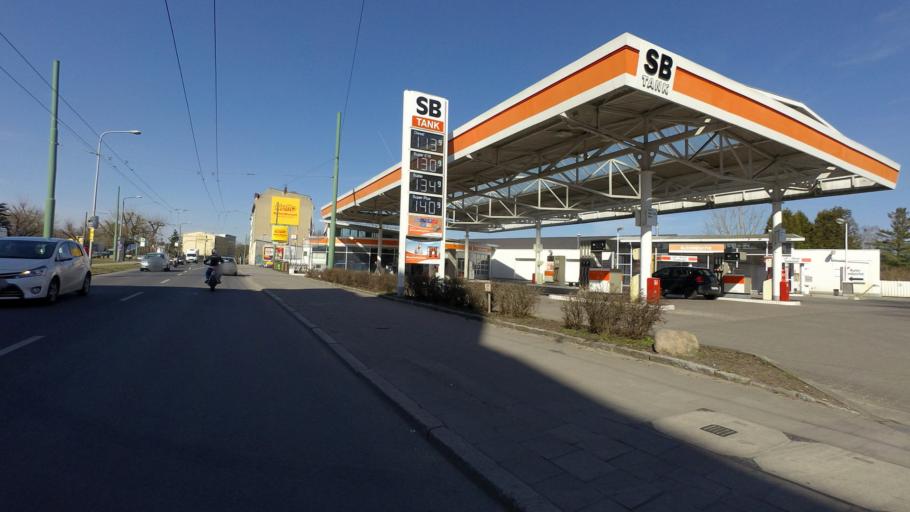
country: DE
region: Brandenburg
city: Eberswalde
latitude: 52.8381
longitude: 13.8199
